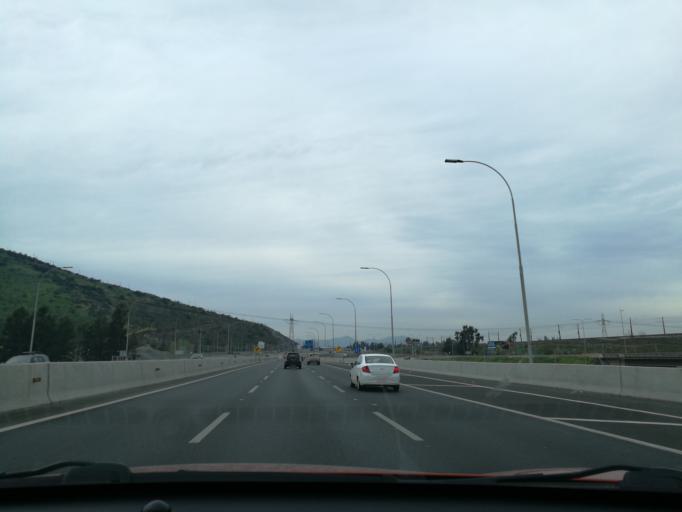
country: CL
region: Santiago Metropolitan
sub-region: Provincia de Maipo
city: Buin
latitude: -33.6902
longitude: -70.7252
